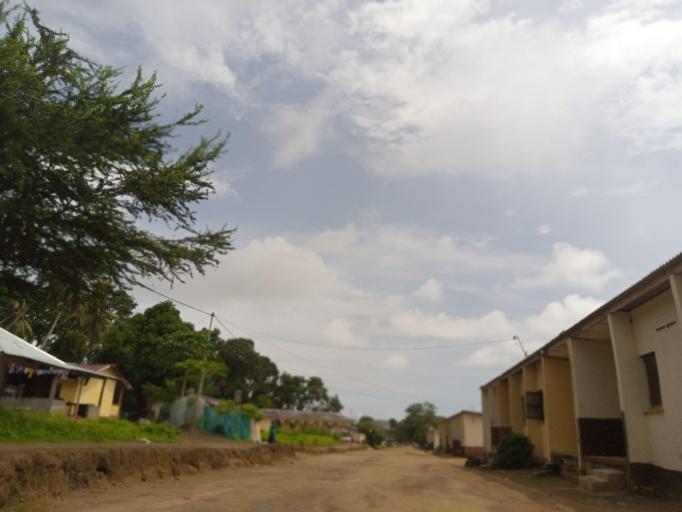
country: SL
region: Northern Province
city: Sawkta
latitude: 8.6285
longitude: -13.2058
